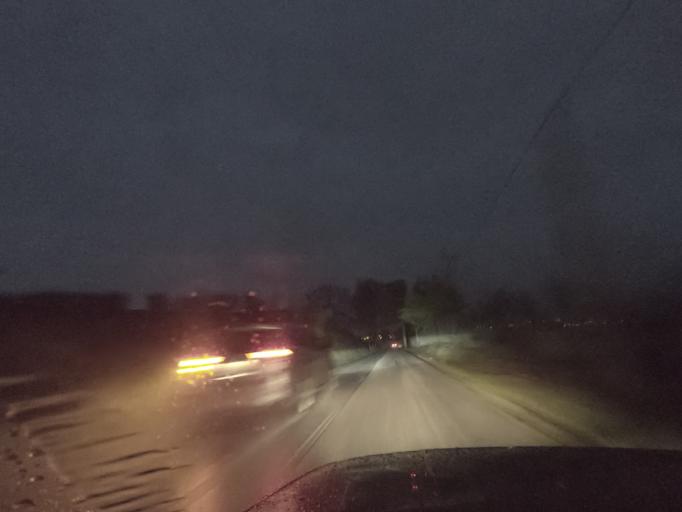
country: PT
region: Vila Real
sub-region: Sabrosa
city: Sabrosa
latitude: 41.2486
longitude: -7.5787
